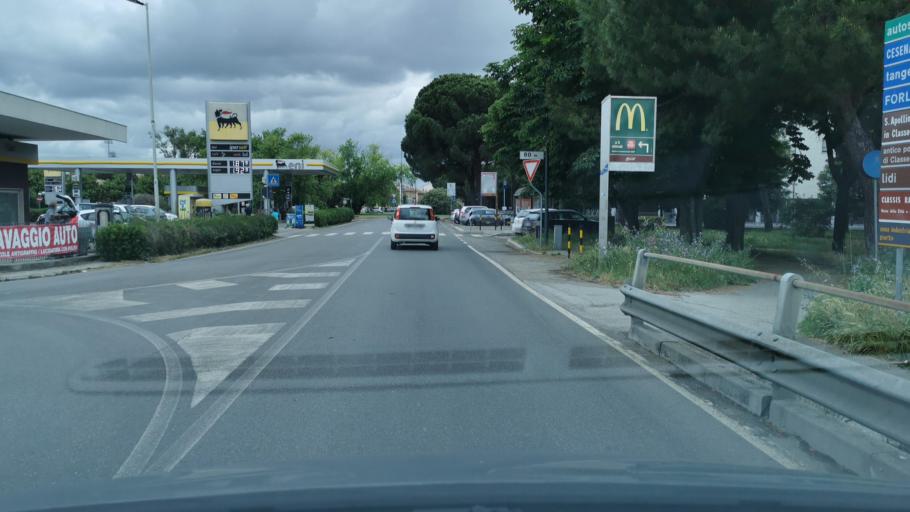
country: IT
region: Emilia-Romagna
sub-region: Provincia di Ravenna
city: Ravenna
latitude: 44.4018
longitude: 12.1970
